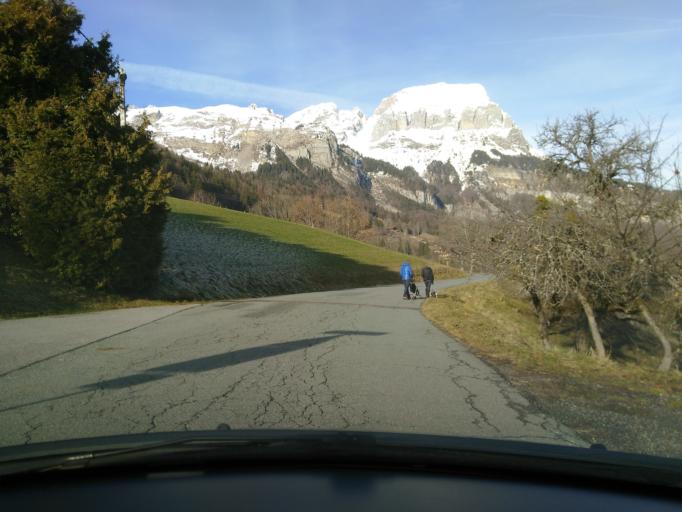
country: FR
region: Rhone-Alpes
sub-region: Departement de la Haute-Savoie
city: Sallanches
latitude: 45.9520
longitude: 6.6177
